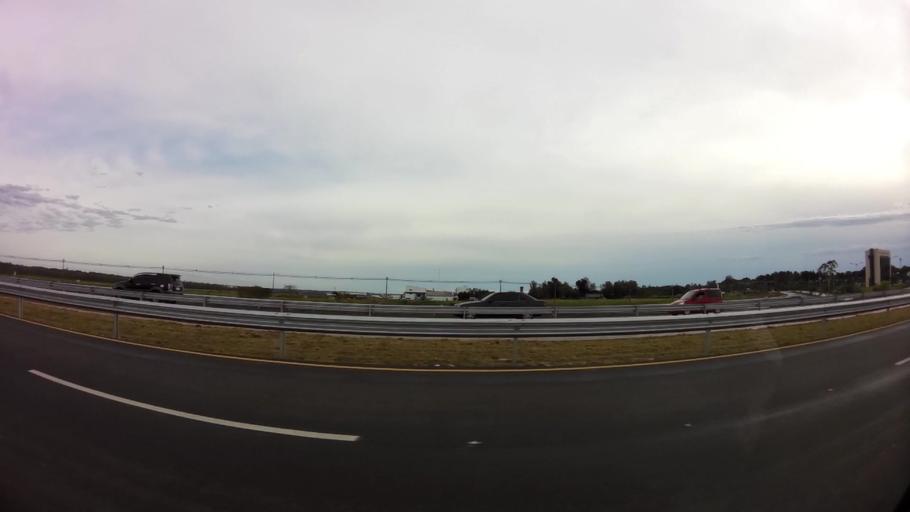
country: PY
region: Central
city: Fernando de la Mora
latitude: -25.2621
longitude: -57.5195
